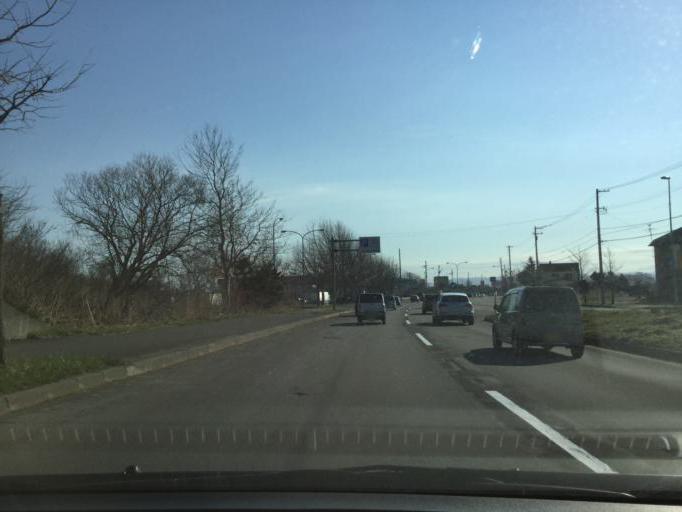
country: JP
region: Hokkaido
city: Iwamizawa
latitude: 43.1867
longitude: 141.7257
